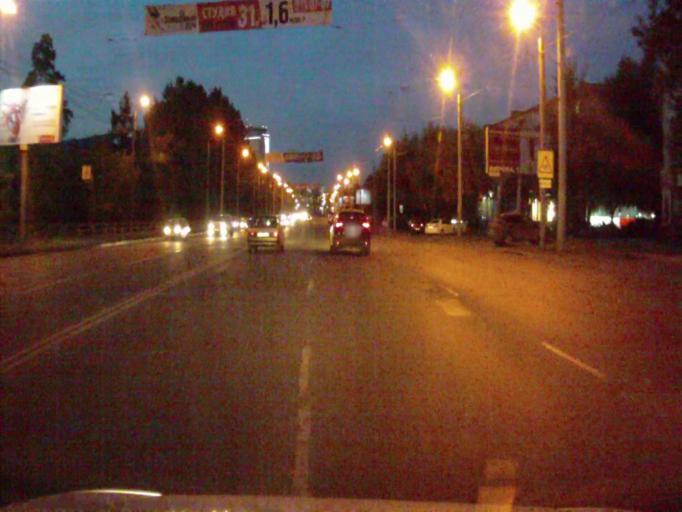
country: RU
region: Chelyabinsk
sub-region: Gorod Chelyabinsk
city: Chelyabinsk
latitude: 55.1631
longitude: 61.3810
